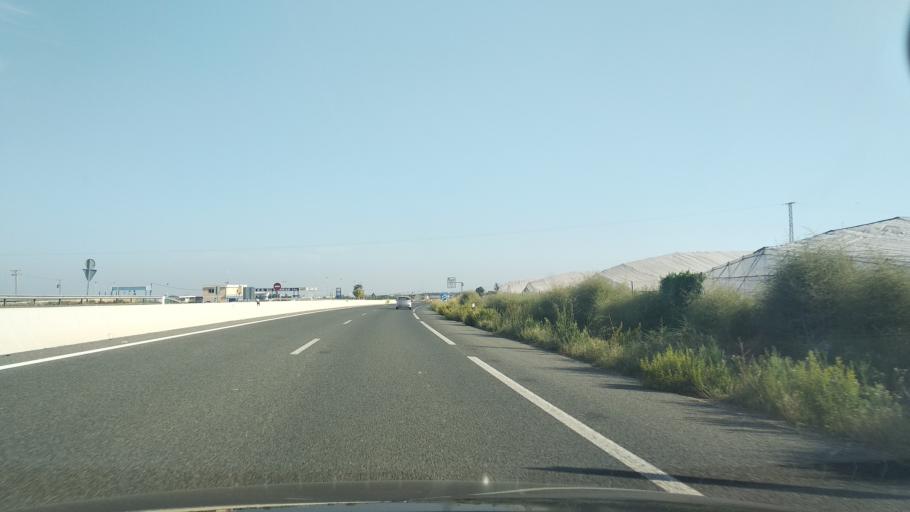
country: ES
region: Murcia
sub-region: Murcia
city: San Javier
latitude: 37.8540
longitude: -0.8824
